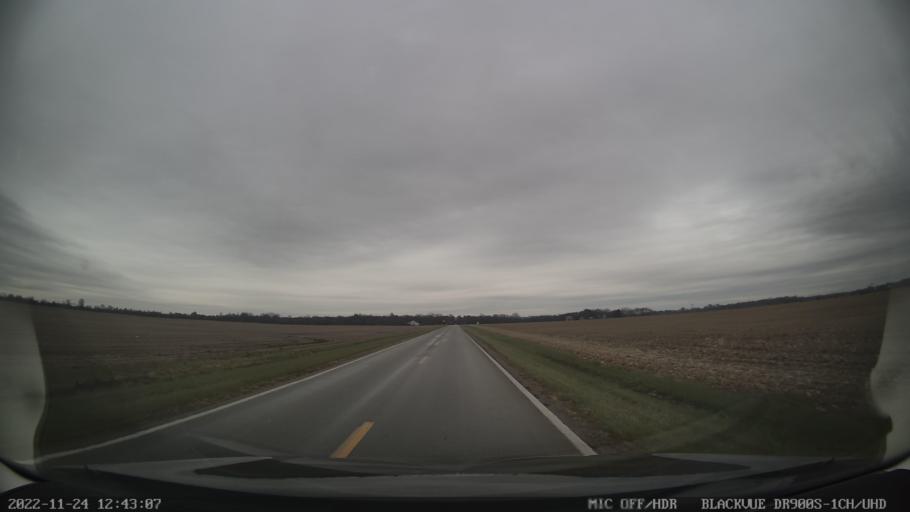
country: US
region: Illinois
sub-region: Macoupin County
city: Staunton
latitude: 38.9615
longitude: -89.7829
